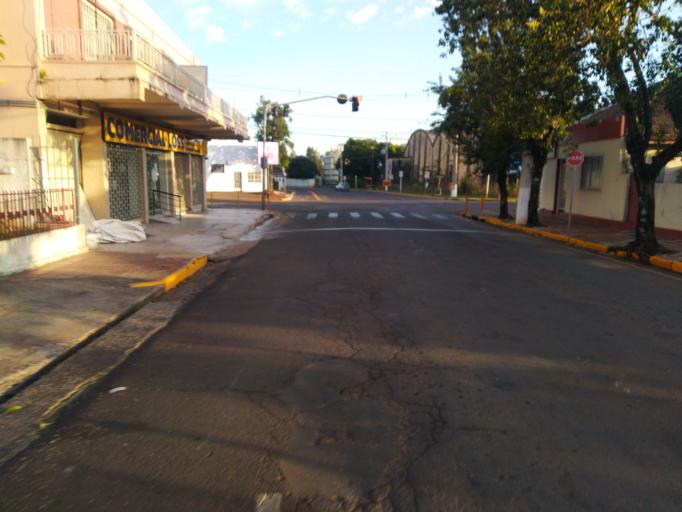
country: BR
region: Rio Grande do Sul
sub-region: Sao Borja
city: Sao Borja
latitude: -28.6502
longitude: -56.0070
